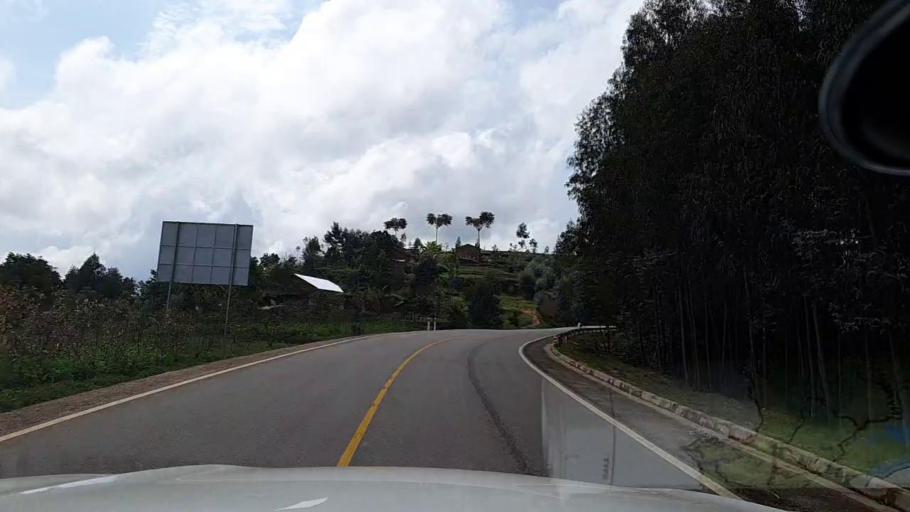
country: RW
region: Southern Province
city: Nzega
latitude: -2.5046
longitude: 29.5010
